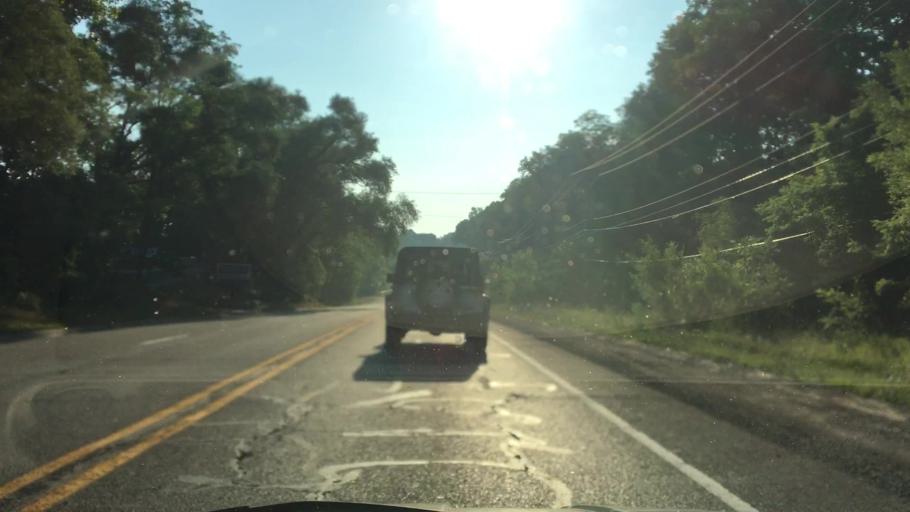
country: US
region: Michigan
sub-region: Livingston County
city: Brighton
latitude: 42.5159
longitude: -83.7126
